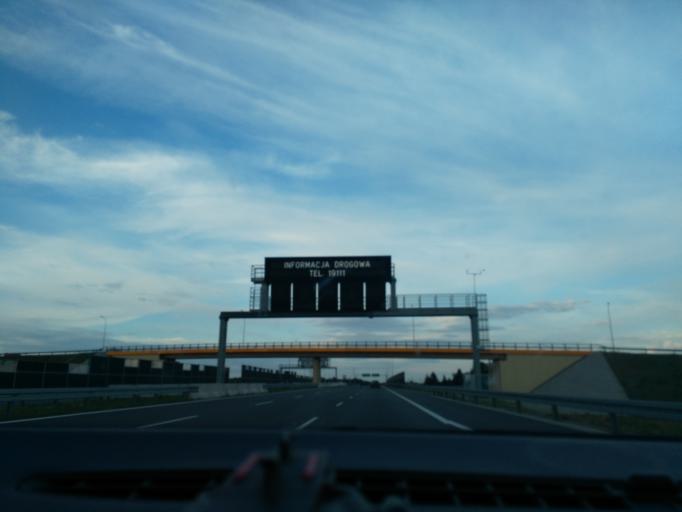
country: PL
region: Lublin Voivodeship
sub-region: Powiat lubelski
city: Lublin
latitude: 51.3008
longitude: 22.5610
